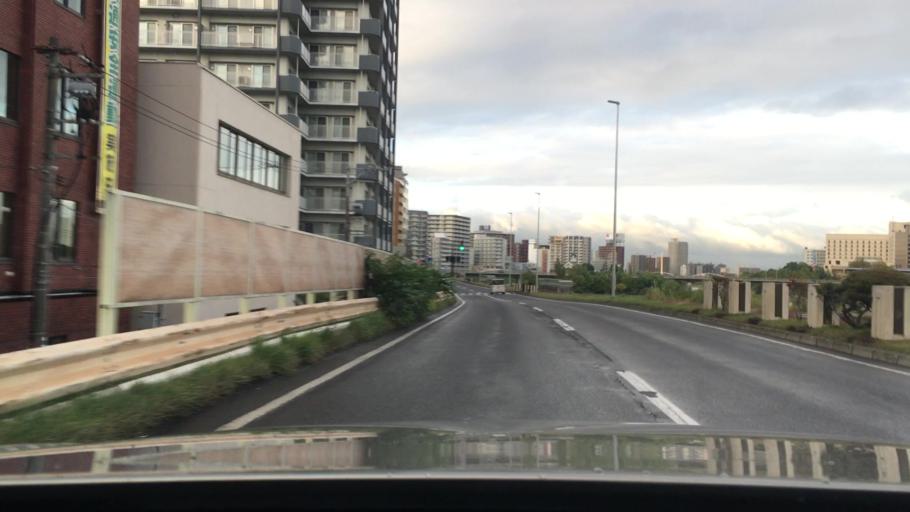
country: JP
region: Hokkaido
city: Sapporo
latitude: 43.0491
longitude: 141.3586
